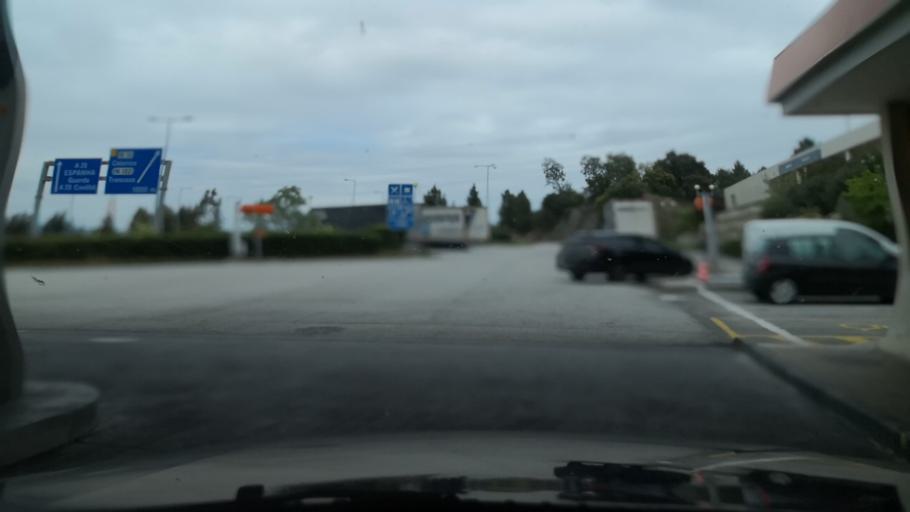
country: PT
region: Guarda
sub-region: Celorico da Beira
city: Celorico da Beira
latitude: 40.6297
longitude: -7.3568
